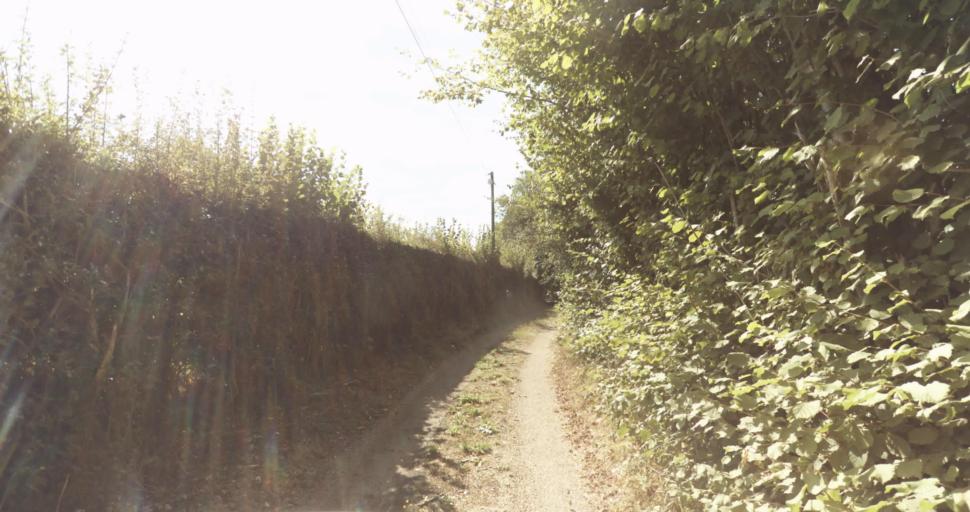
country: FR
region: Lower Normandy
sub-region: Departement de l'Orne
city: Vimoutiers
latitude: 48.9306
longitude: 0.2357
